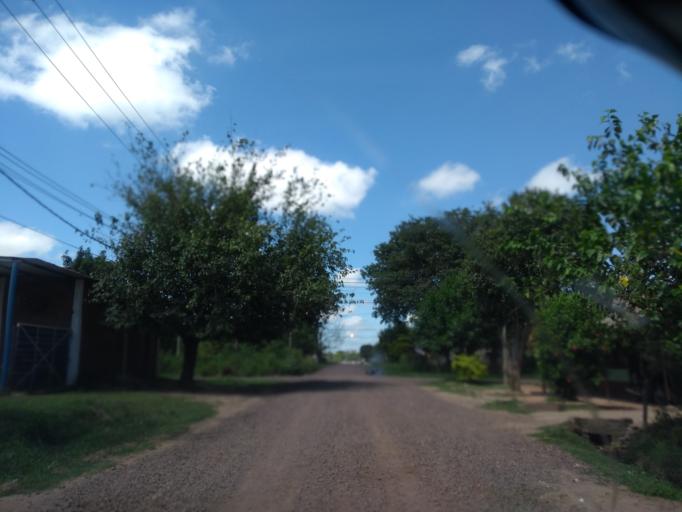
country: AR
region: Chaco
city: Fontana
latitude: -27.4068
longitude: -59.0416
